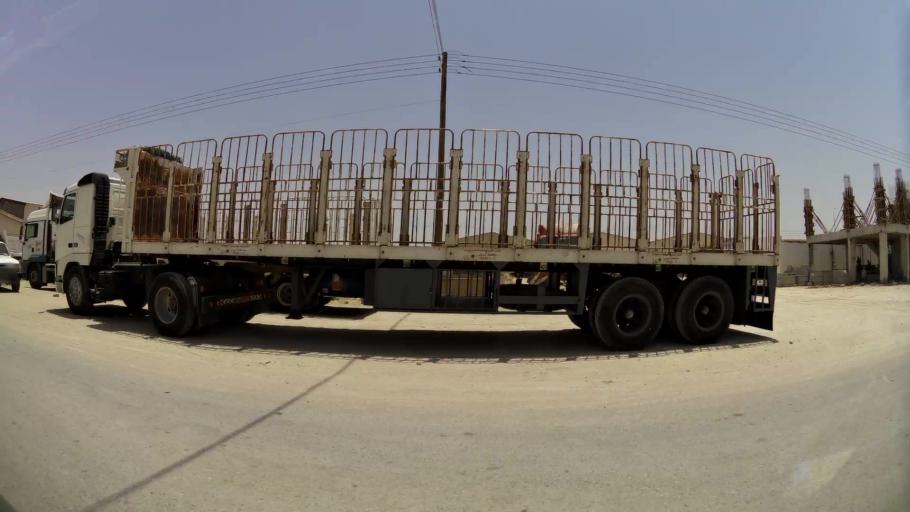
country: OM
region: Zufar
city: Salalah
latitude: 17.0224
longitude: 54.1179
